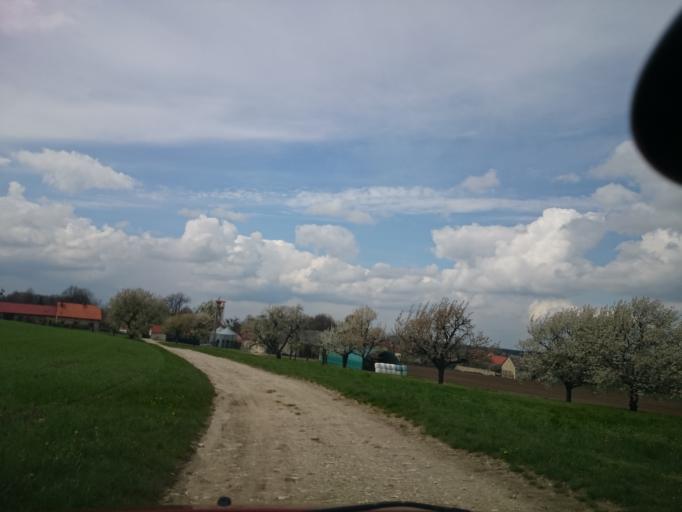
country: PL
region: Opole Voivodeship
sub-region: Powiat krapkowicki
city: Rozwadza
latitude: 50.4894
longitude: 18.1242
